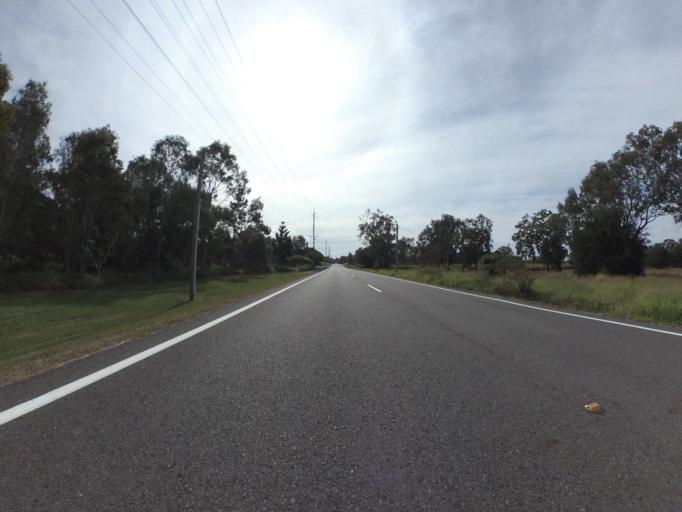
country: AU
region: Queensland
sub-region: Brisbane
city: Moggill
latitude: -27.5874
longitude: 152.8610
